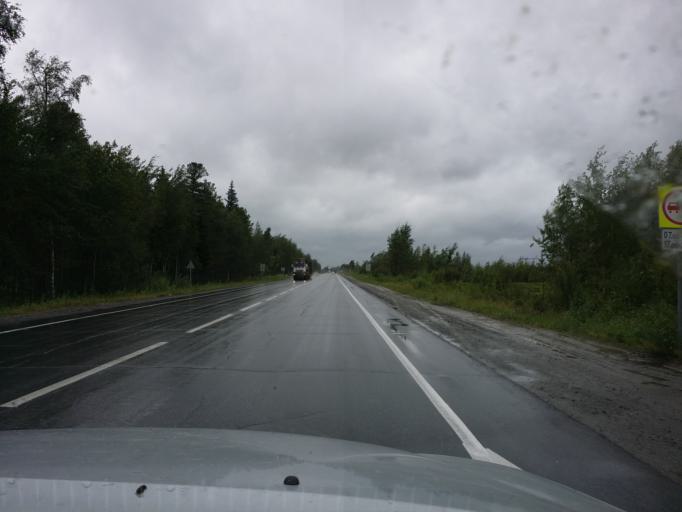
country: RU
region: Khanty-Mansiyskiy Avtonomnyy Okrug
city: Megion
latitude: 61.0649
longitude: 76.2644
